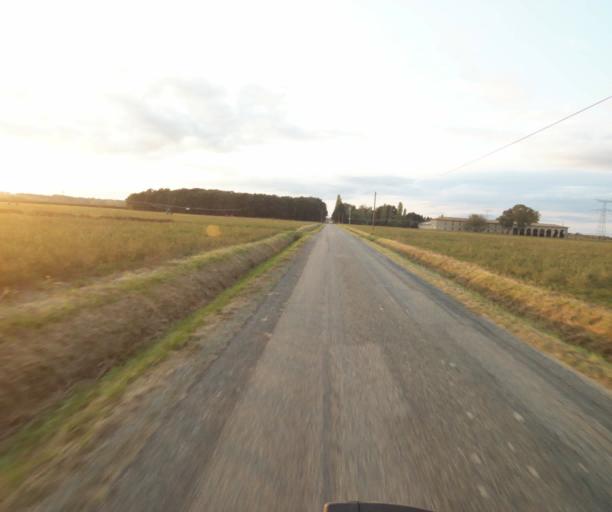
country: FR
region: Midi-Pyrenees
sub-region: Departement du Tarn-et-Garonne
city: Verdun-sur-Garonne
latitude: 43.8273
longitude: 1.2327
